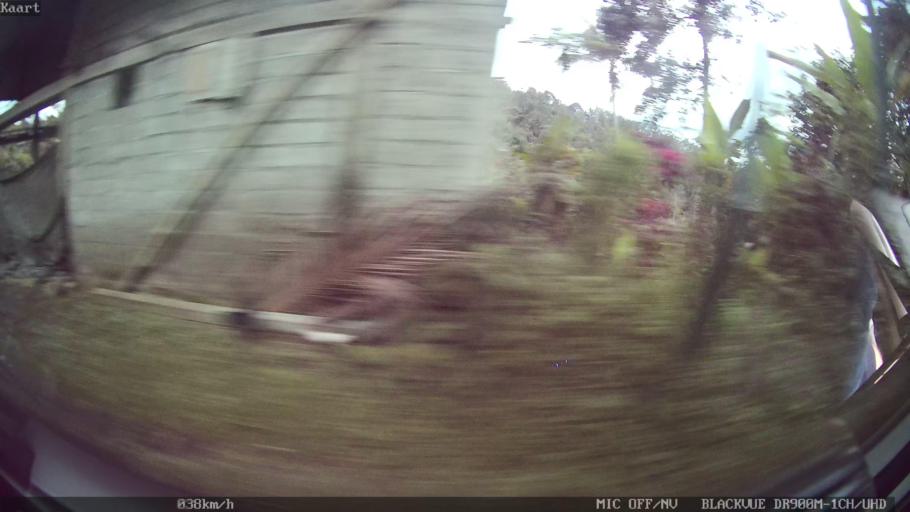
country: ID
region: Bali
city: Peneng
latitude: -8.3628
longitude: 115.1791
